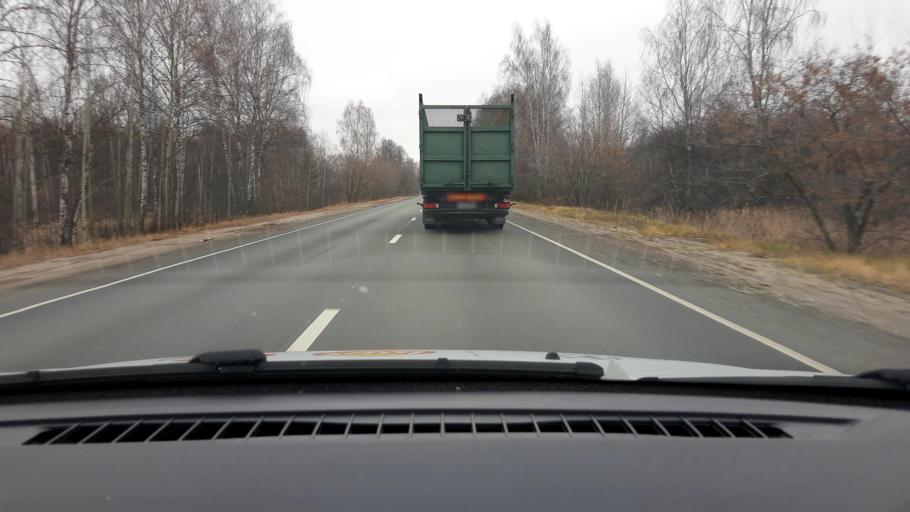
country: RU
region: Nizjnij Novgorod
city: Gorodets
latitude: 56.5719
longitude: 43.4792
